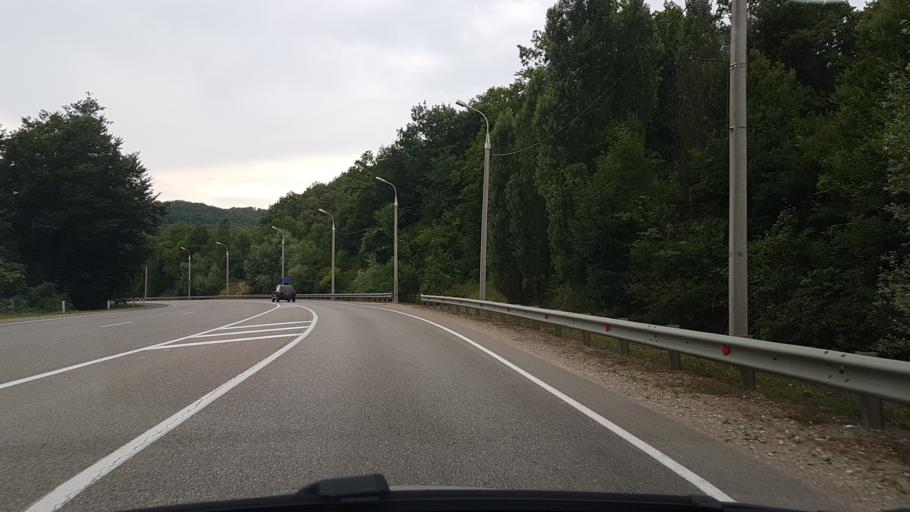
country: RU
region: Krasnodarskiy
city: Lermontovo
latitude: 44.4709
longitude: 38.8775
